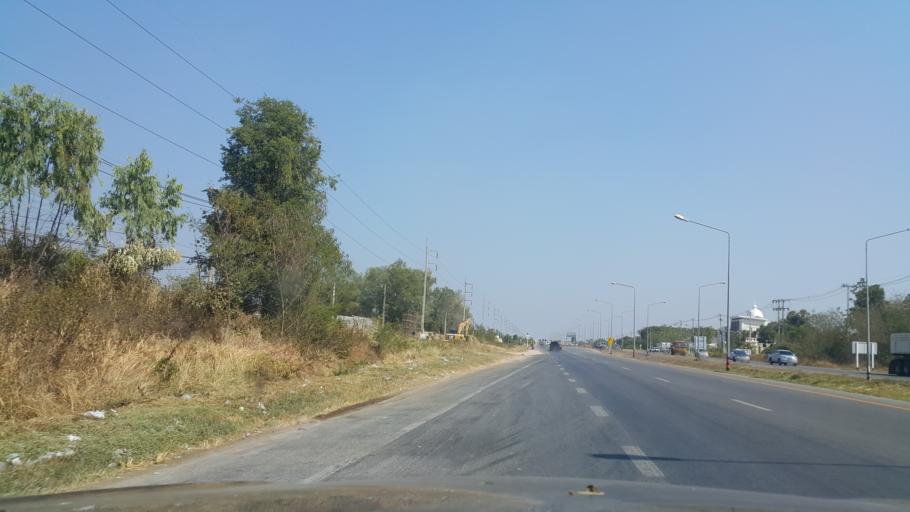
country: TH
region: Khon Kaen
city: Khon Kaen
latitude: 16.5118
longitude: 102.8366
